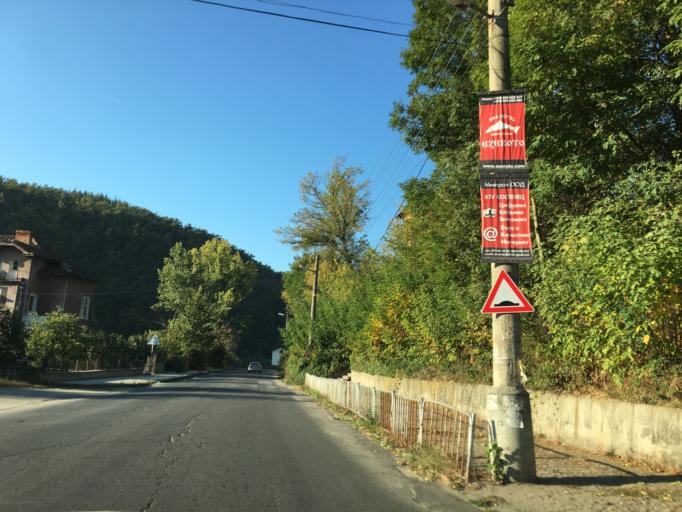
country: BG
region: Sofiya
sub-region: Obshtina Dolna Banya
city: Dolna Banya
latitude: 42.3275
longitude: 23.8706
